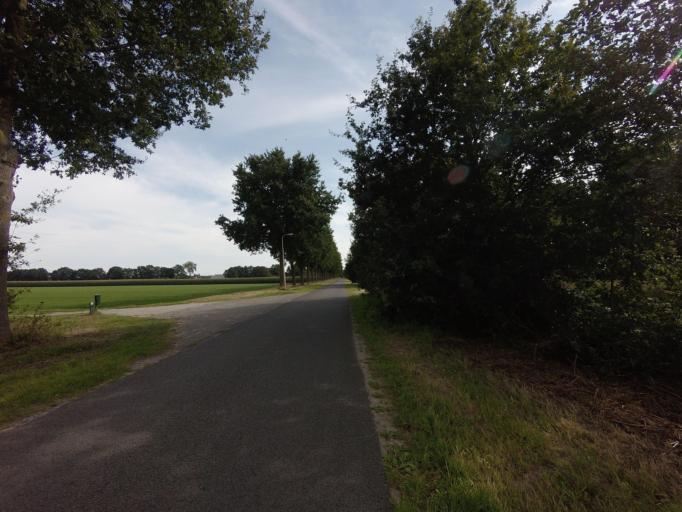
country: NL
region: Drenthe
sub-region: Gemeente Coevorden
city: Coevorden
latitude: 52.6836
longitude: 6.7138
